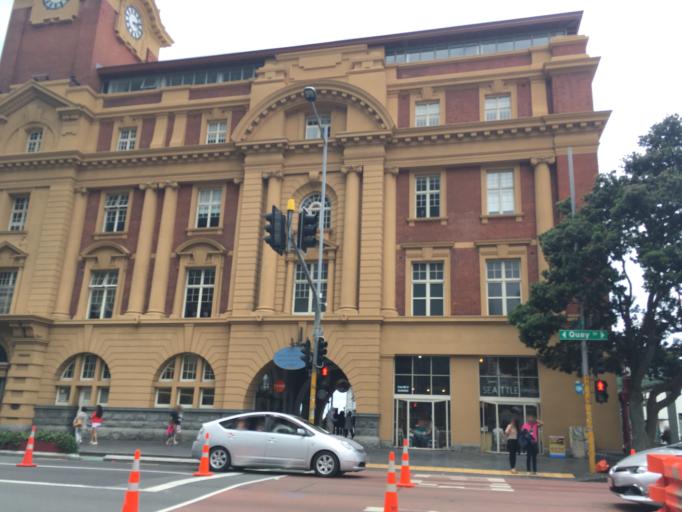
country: NZ
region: Auckland
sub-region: Auckland
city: Auckland
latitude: -36.8433
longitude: 174.7671
